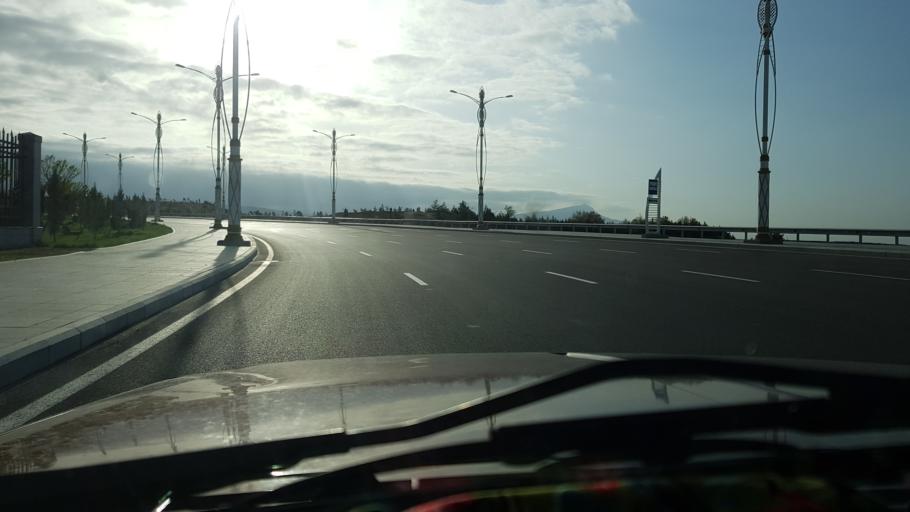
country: TM
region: Ahal
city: Ashgabat
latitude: 37.9311
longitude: 58.3338
